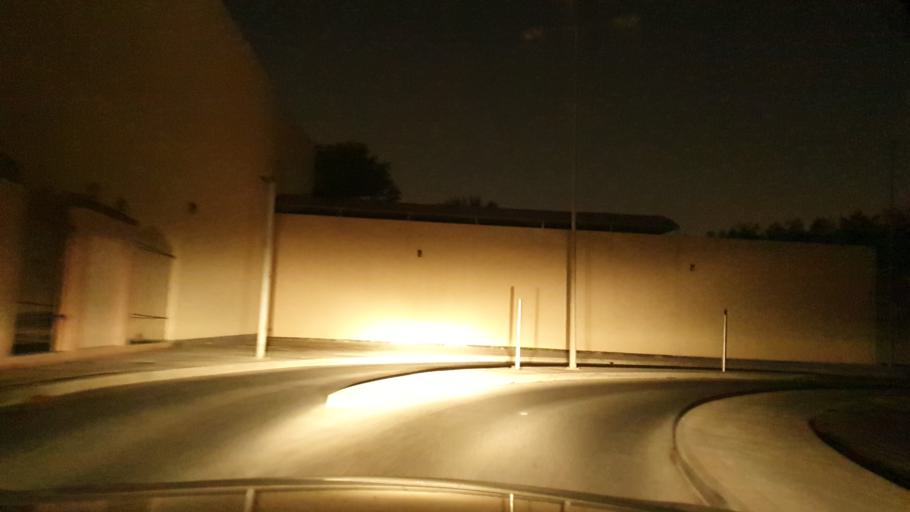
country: BH
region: Manama
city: Jidd Hafs
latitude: 26.1994
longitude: 50.5470
